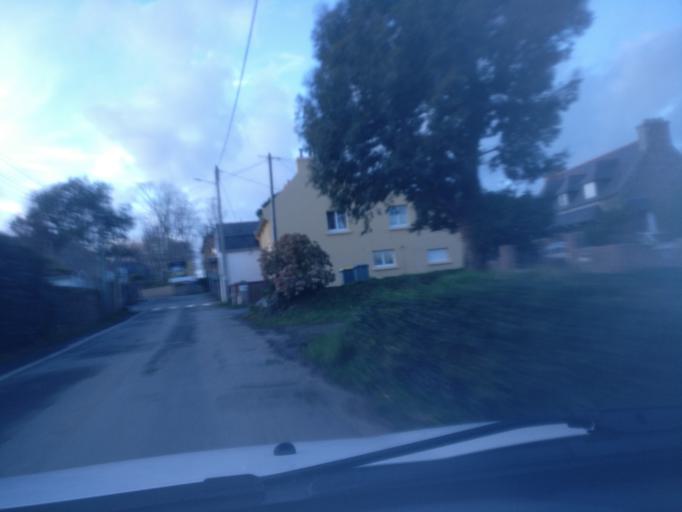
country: FR
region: Brittany
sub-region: Departement des Cotes-d'Armor
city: Perros-Guirec
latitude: 48.8185
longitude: -3.4661
